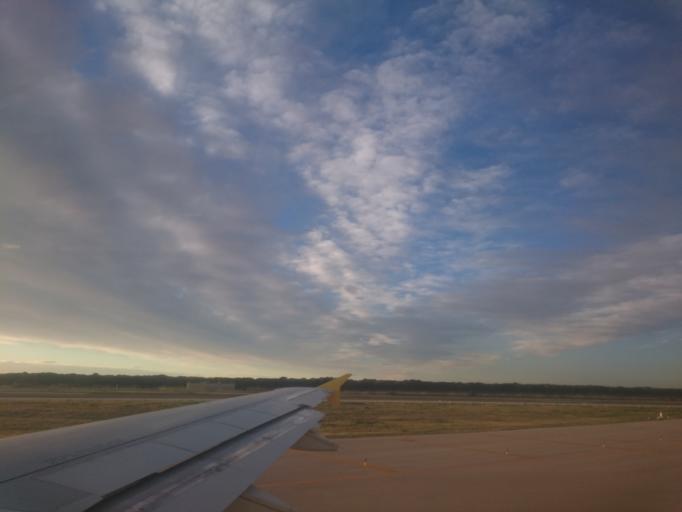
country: ES
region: Catalonia
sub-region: Provincia de Barcelona
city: El Prat de Llobregat
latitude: 41.2919
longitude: 2.0970
